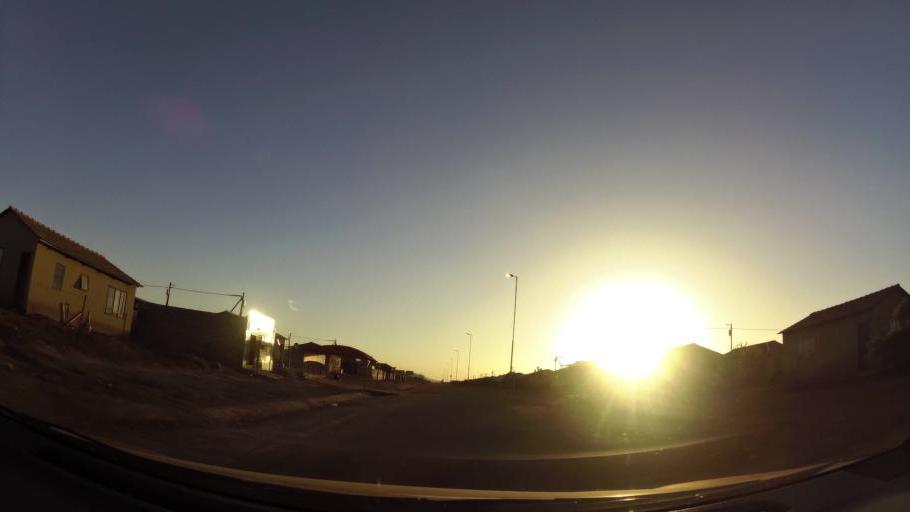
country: ZA
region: North-West
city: Ga-Rankuwa
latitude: -25.6030
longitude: 28.0892
